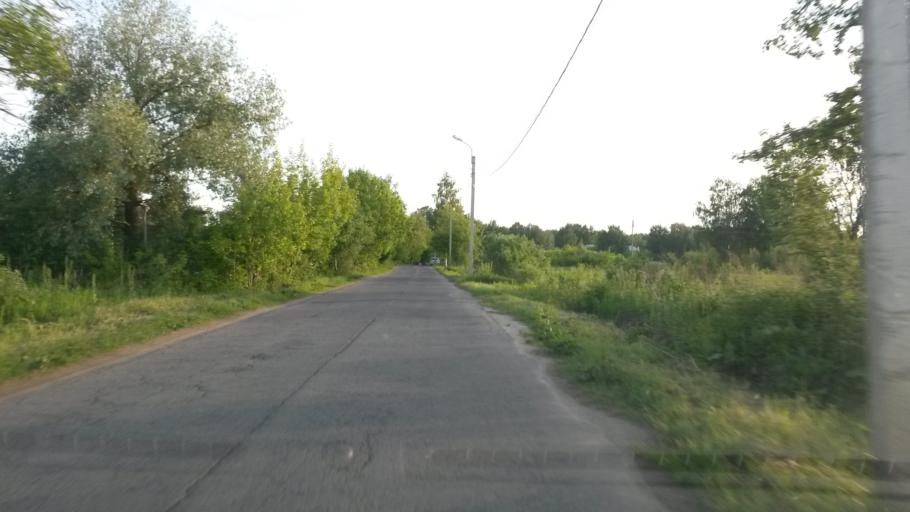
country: RU
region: Jaroslavl
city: Yaroslavl
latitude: 57.7030
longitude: 39.8290
